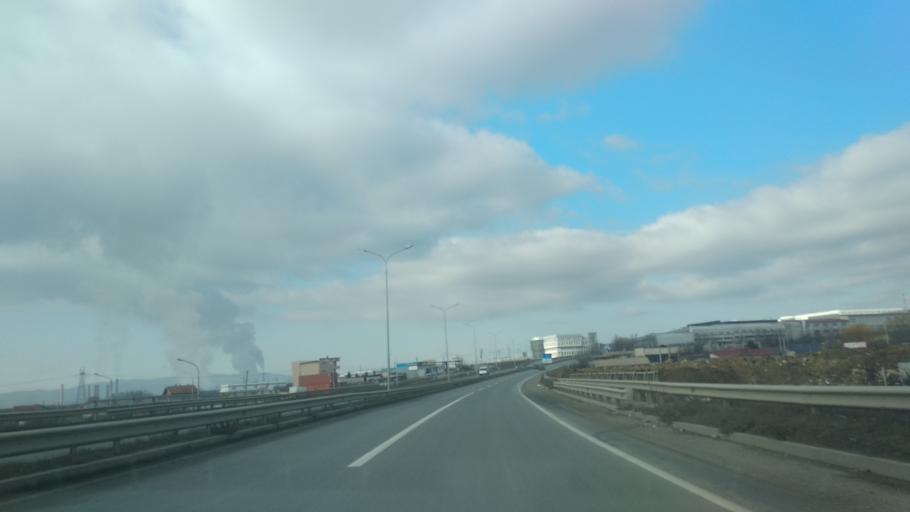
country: XK
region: Pristina
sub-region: Kosovo Polje
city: Kosovo Polje
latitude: 42.6692
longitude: 21.1197
